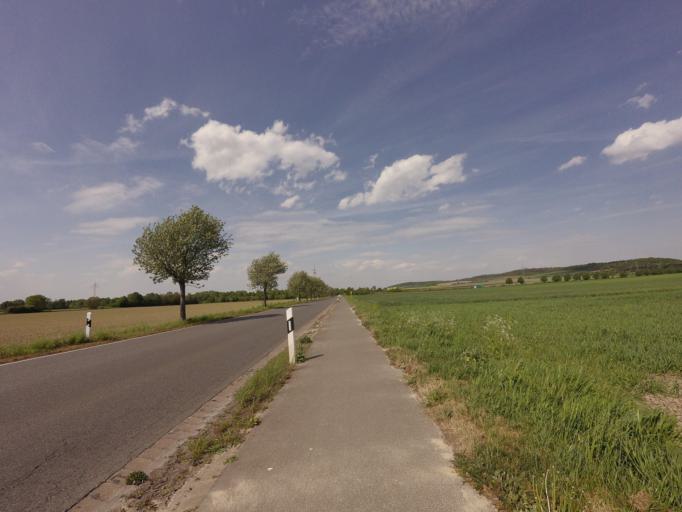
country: DE
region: Lower Saxony
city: Giesen
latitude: 52.1541
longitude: 9.8793
